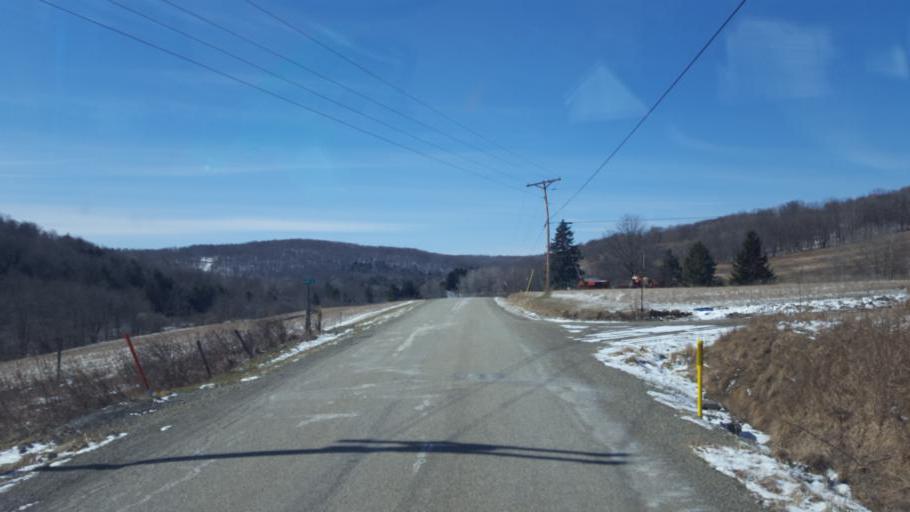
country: US
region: New York
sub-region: Allegany County
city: Andover
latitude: 41.9488
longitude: -77.8024
